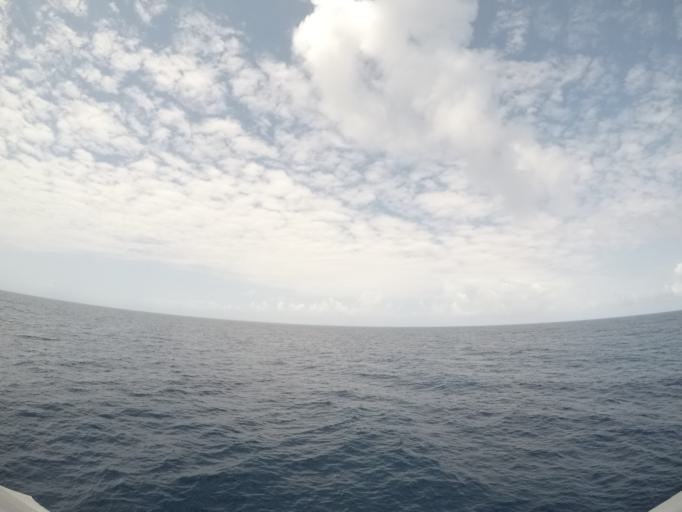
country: TZ
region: Zanzibar North
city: Nungwi
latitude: -5.5774
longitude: 39.3617
